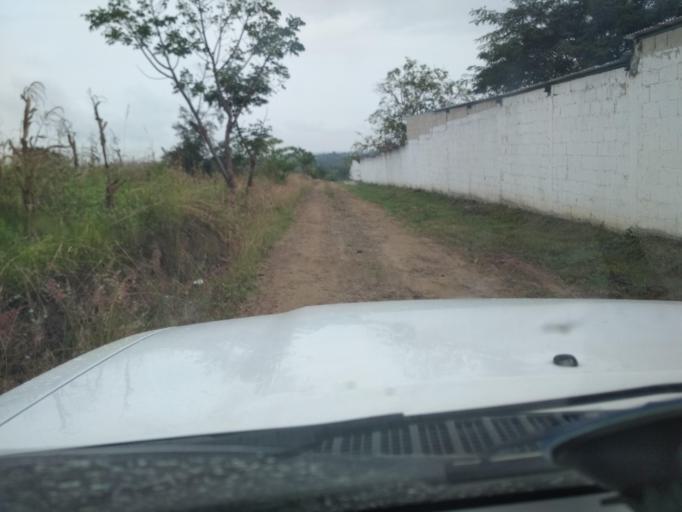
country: MX
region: Veracruz
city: El Castillo
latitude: 19.5362
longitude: -96.8251
